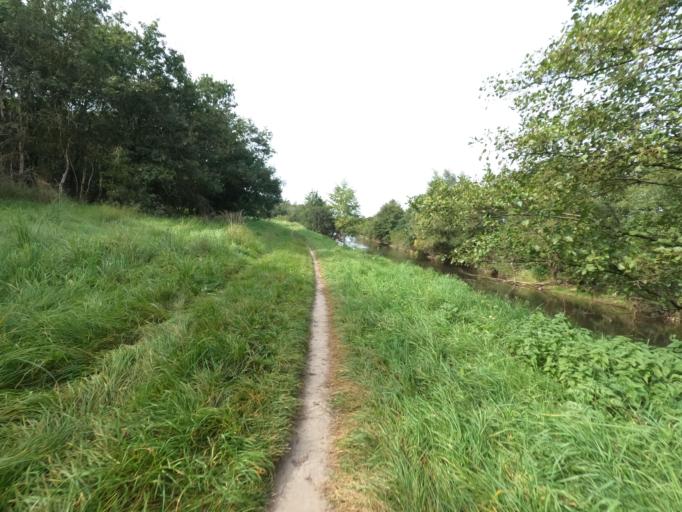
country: DE
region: North Rhine-Westphalia
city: Huckelhoven
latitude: 51.0270
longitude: 6.2399
